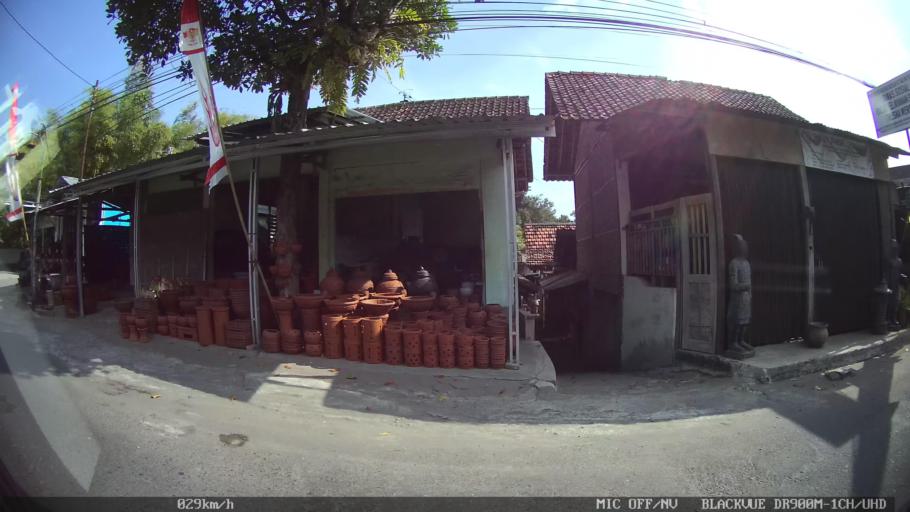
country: ID
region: Daerah Istimewa Yogyakarta
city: Kasihan
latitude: -7.8454
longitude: 110.3376
